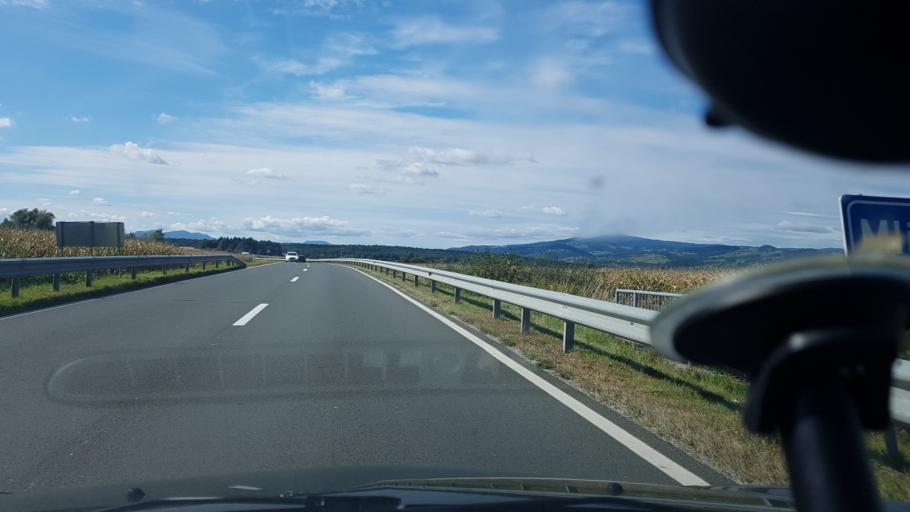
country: SI
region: Slovenska Bistrica
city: Pragersko
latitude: 46.4056
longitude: 15.6616
